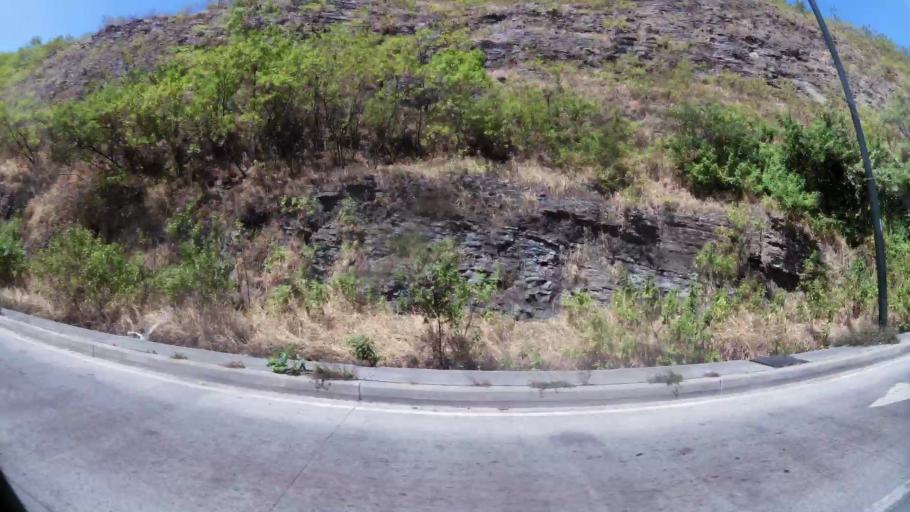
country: EC
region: Guayas
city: Guayaquil
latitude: -2.1814
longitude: -79.9282
